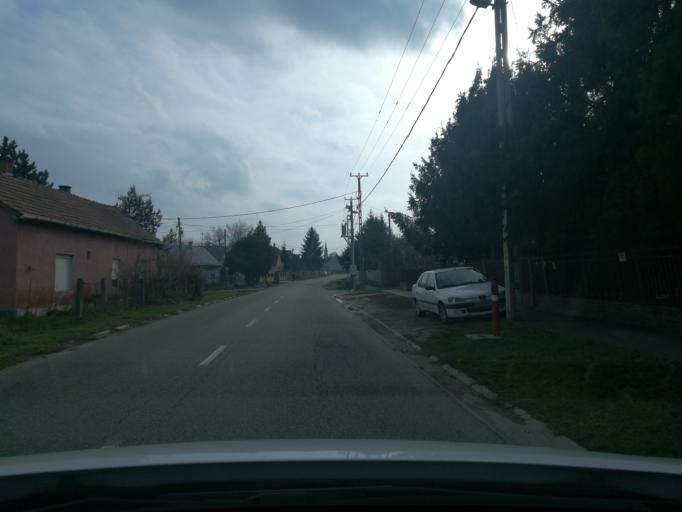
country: HU
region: Szabolcs-Szatmar-Bereg
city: Nyirpazony
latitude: 47.9631
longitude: 21.8017
